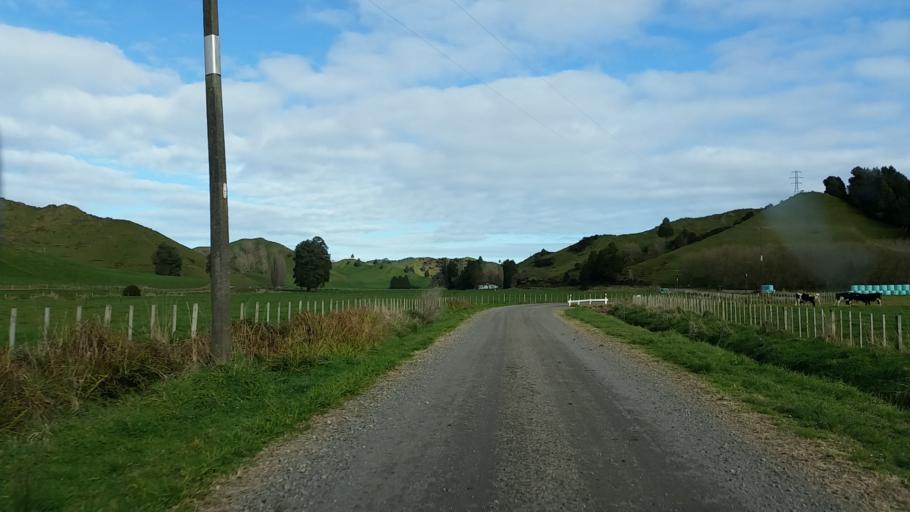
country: NZ
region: Taranaki
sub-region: South Taranaki District
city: Eltham
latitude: -39.2505
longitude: 174.5378
